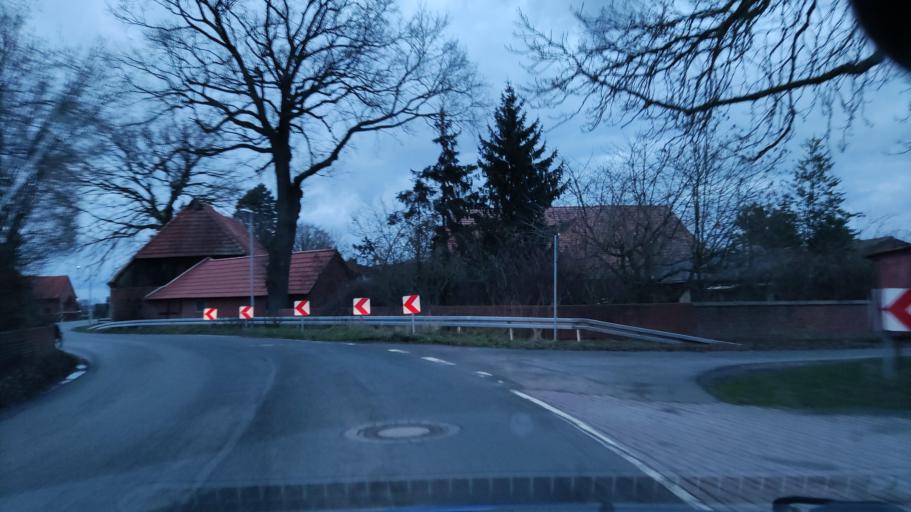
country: DE
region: Lower Saxony
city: Schwarmstedt
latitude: 52.6331
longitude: 9.5743
